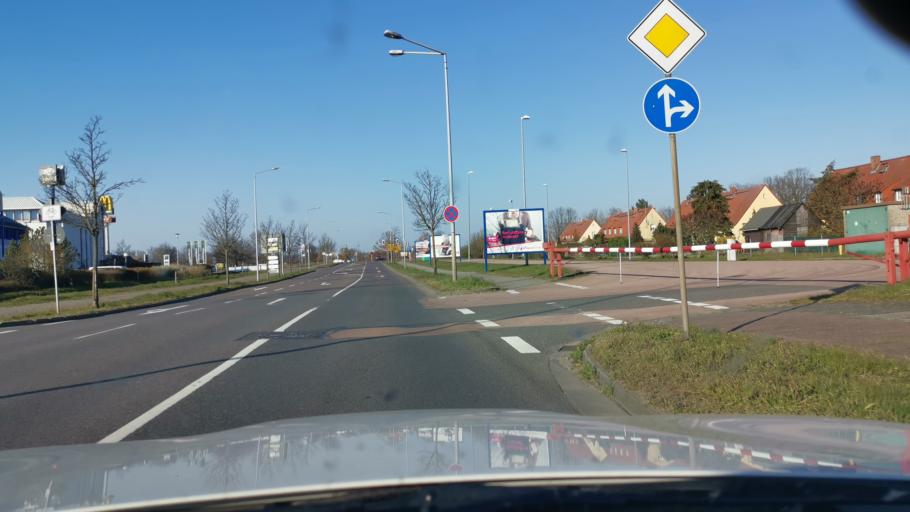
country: DE
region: Saxony-Anhalt
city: Vockerode
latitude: 51.8217
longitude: 12.3006
